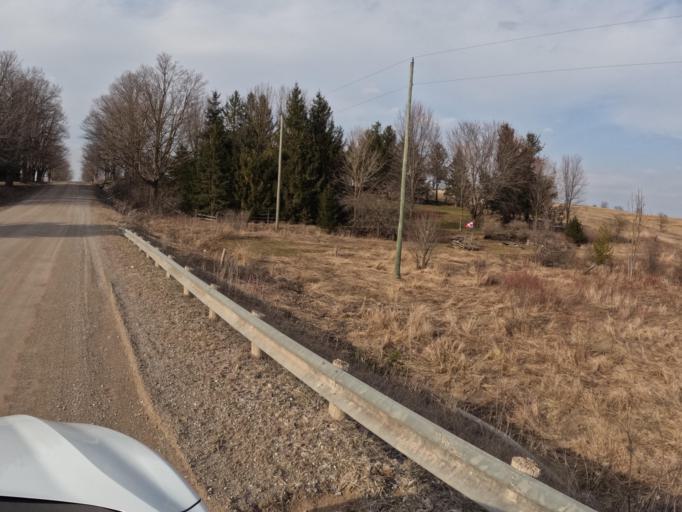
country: CA
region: Ontario
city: Orangeville
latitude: 43.8970
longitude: -80.2670
